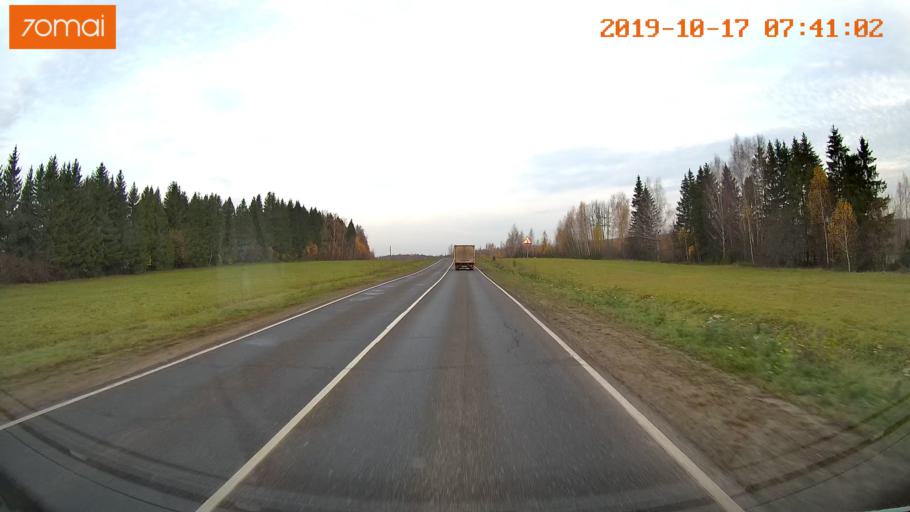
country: RU
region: Vladimir
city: Yur'yev-Pol'skiy
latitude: 56.4788
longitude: 39.8184
